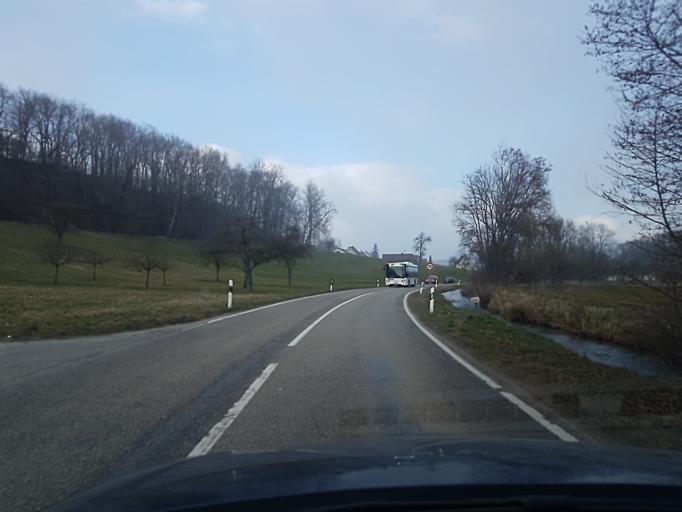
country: DE
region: Baden-Wuerttemberg
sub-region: Regierungsbezirk Stuttgart
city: Eberdingen
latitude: 48.9075
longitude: 8.9785
